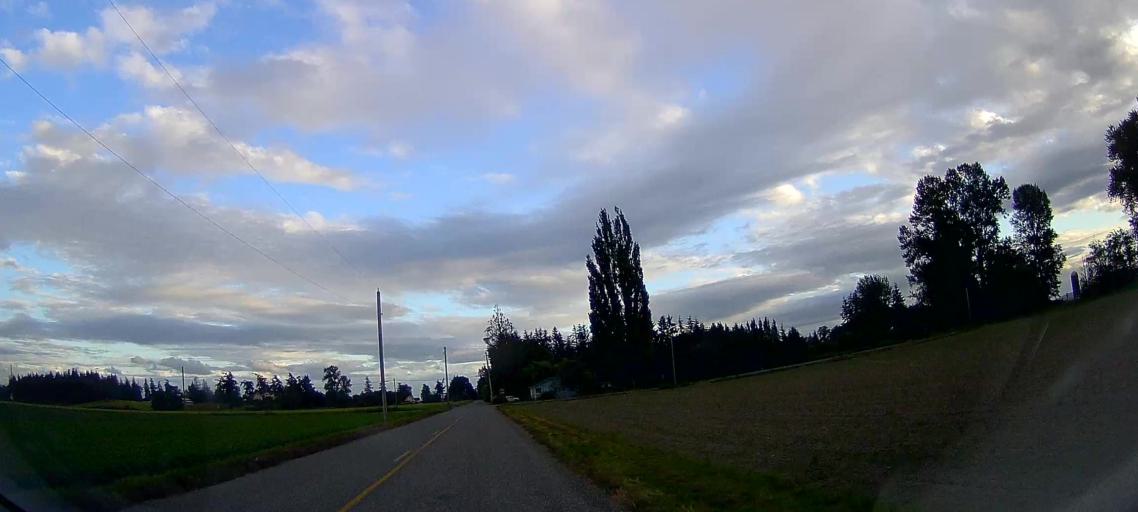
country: US
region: Washington
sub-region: Skagit County
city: Mount Vernon
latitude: 48.3712
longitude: -122.3789
